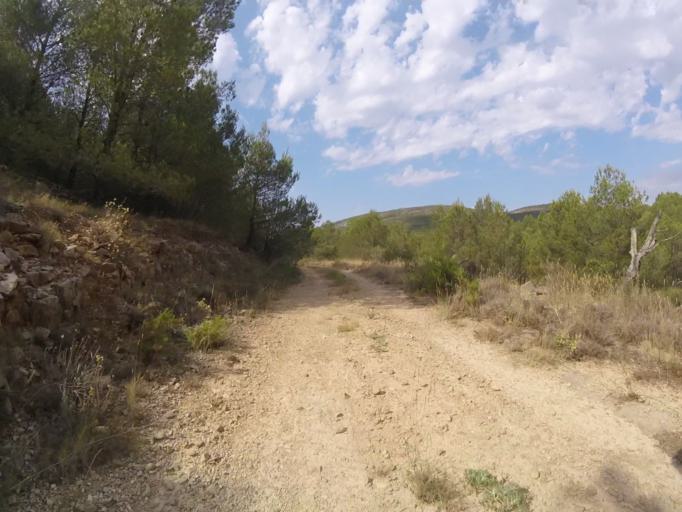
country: ES
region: Valencia
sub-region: Provincia de Castello
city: Alcala de Xivert
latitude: 40.3574
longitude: 0.1990
